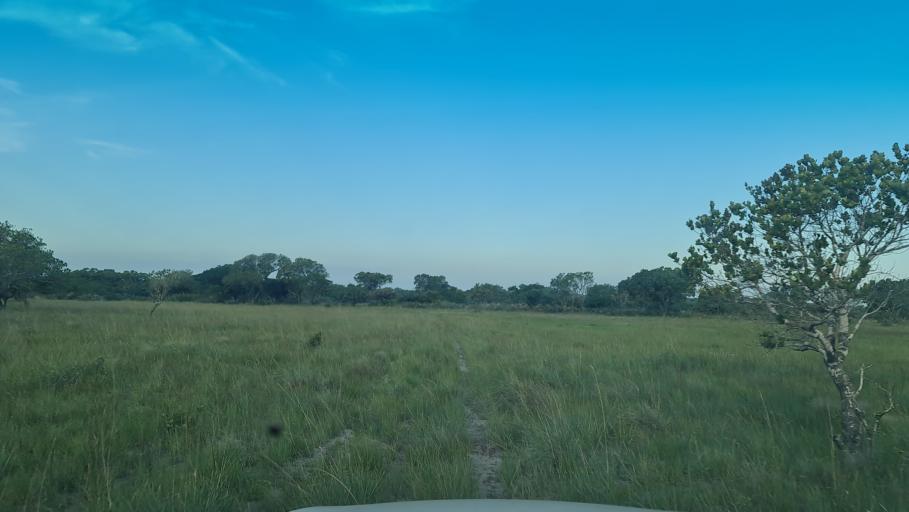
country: MZ
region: Gaza
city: Macia
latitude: -25.2140
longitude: 33.0537
